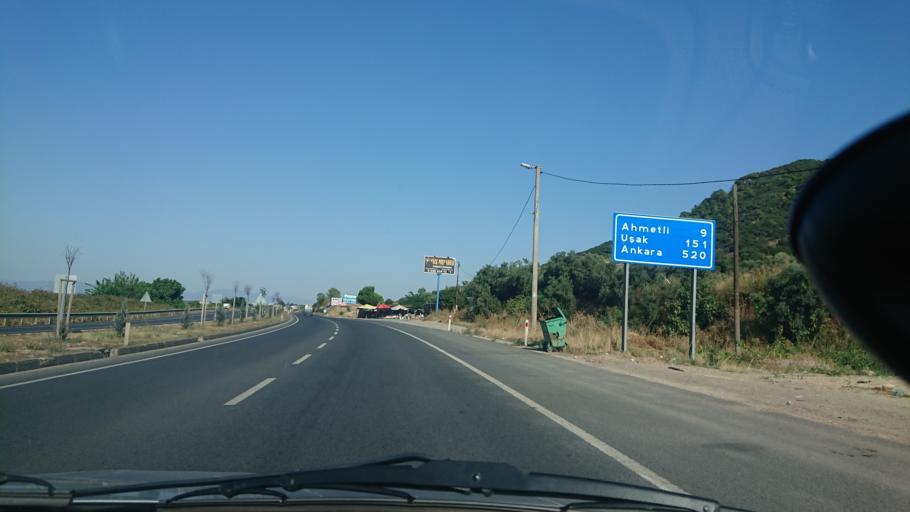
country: TR
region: Manisa
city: Ahmetli
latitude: 38.4908
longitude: 27.8448
